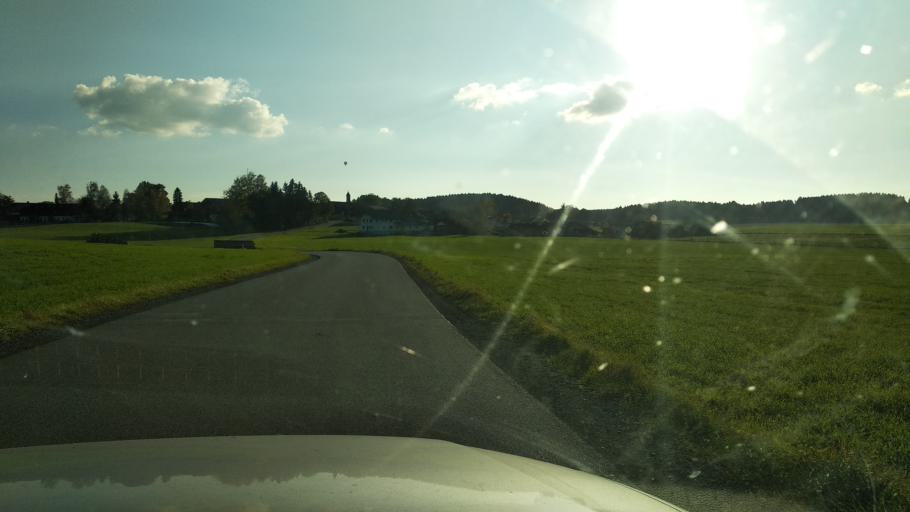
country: DE
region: Bavaria
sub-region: Upper Bavaria
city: Glonn
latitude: 47.9747
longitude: 11.8393
